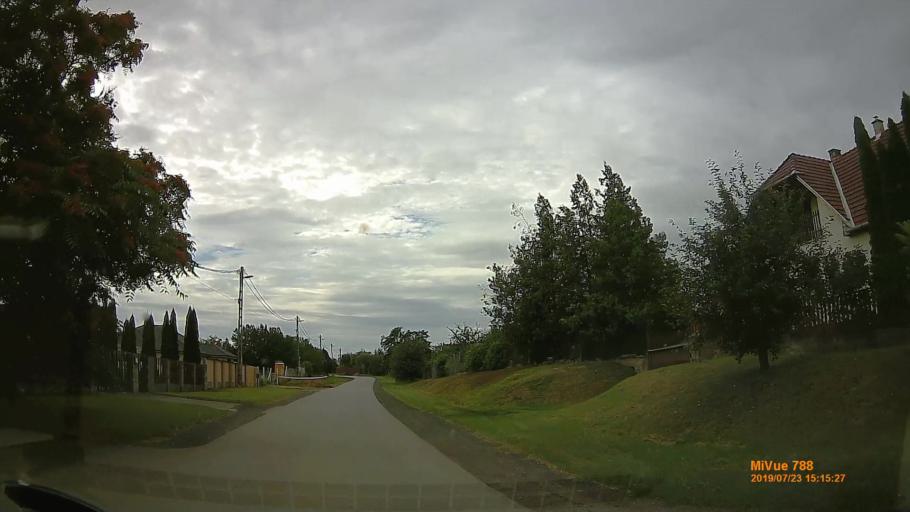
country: HU
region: Szabolcs-Szatmar-Bereg
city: Nyiregyhaza
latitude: 47.9135
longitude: 21.7625
